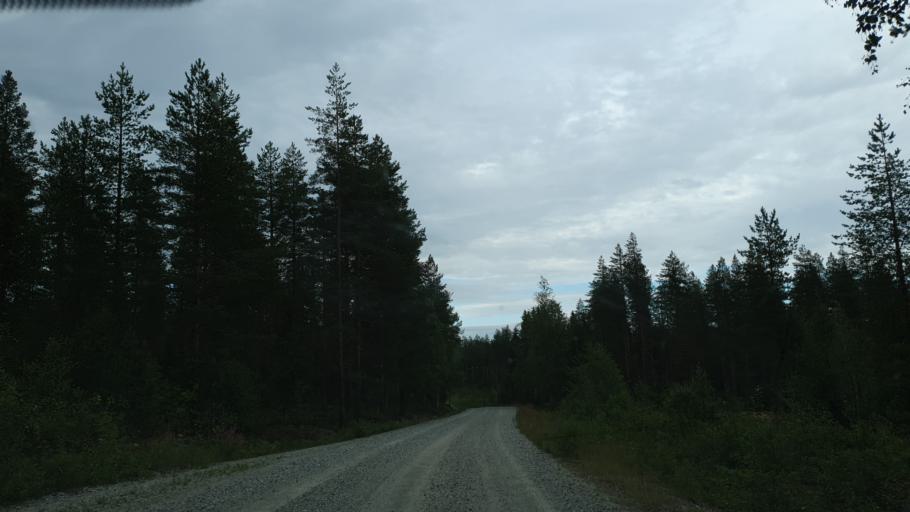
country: FI
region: Kainuu
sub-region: Kehys-Kainuu
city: Kuhmo
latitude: 64.4527
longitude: 29.5703
